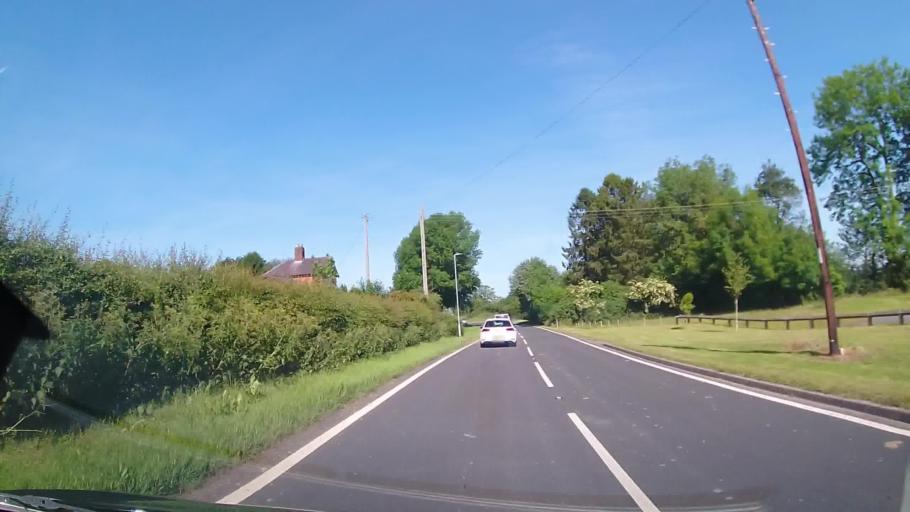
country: GB
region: Wales
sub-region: Sir Powys
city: Llanfyllin
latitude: 52.6609
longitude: -3.2711
